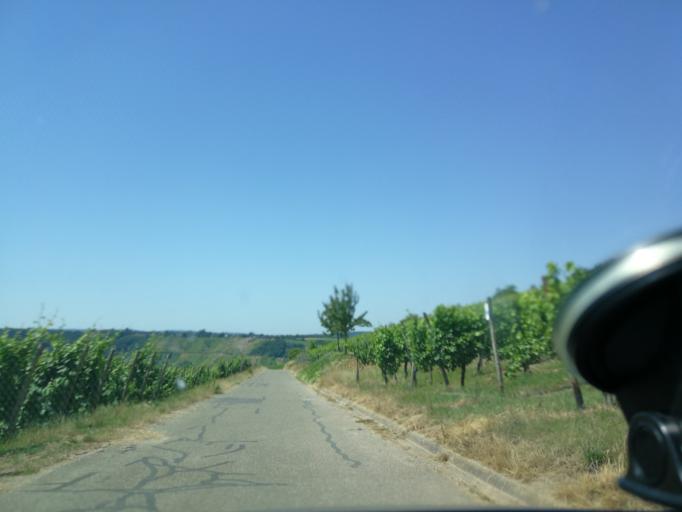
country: DE
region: Rheinland-Pfalz
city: Minheim
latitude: 49.8768
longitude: 6.9377
